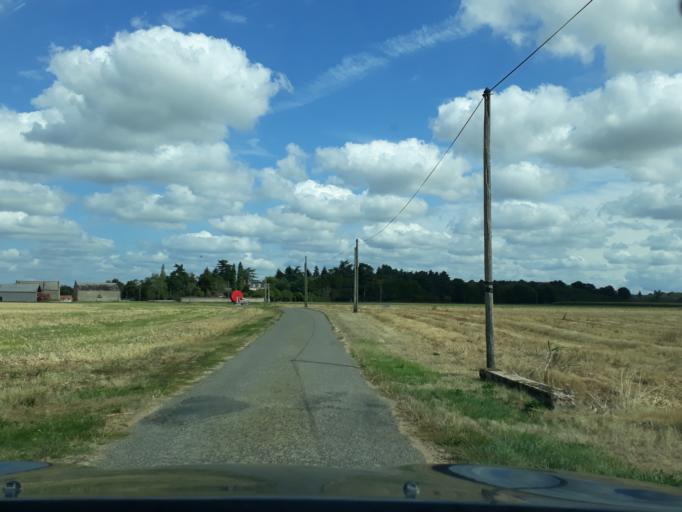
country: FR
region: Centre
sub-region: Departement du Loiret
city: Saint-Cyr-en-Val
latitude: 47.8424
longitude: 1.9840
